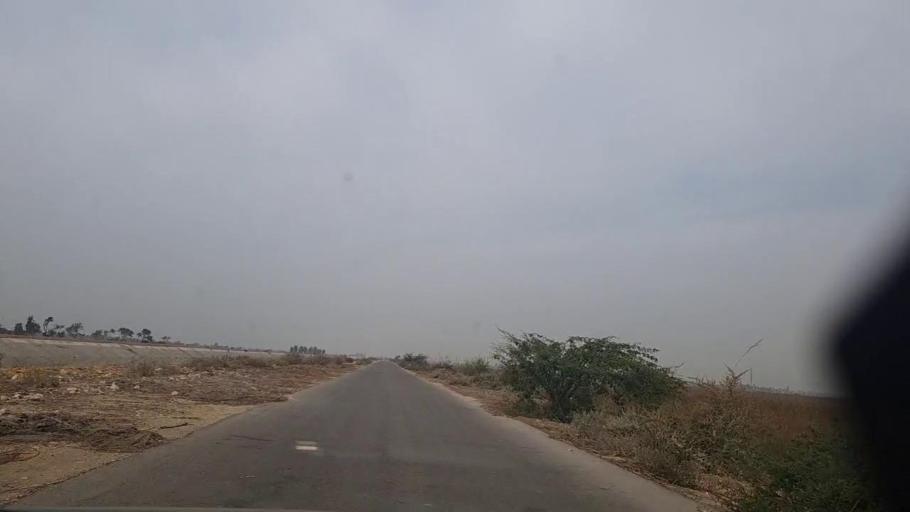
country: PK
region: Sindh
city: Sakrand
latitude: 26.2638
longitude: 68.2405
